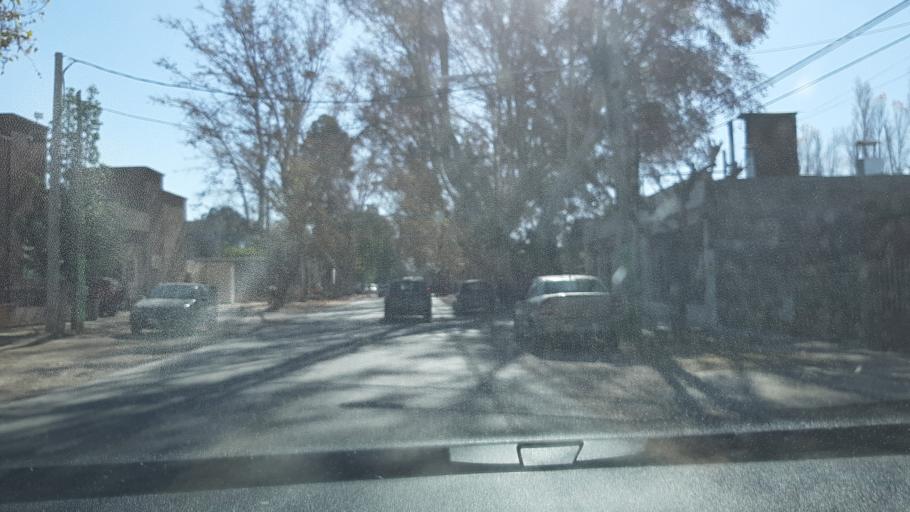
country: AR
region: San Juan
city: San Juan
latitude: -31.5257
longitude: -68.5954
